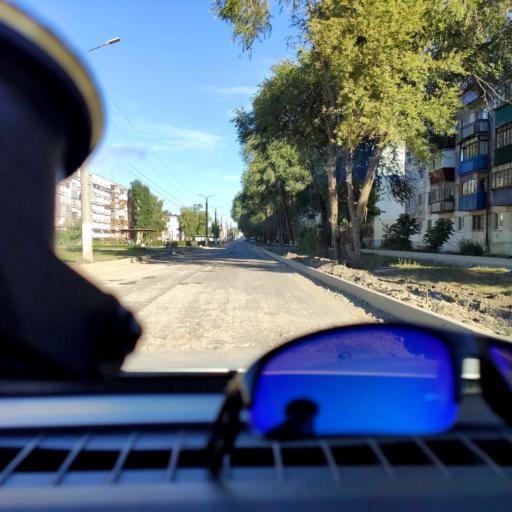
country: RU
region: Samara
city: Chapayevsk
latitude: 52.9513
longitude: 49.6954
